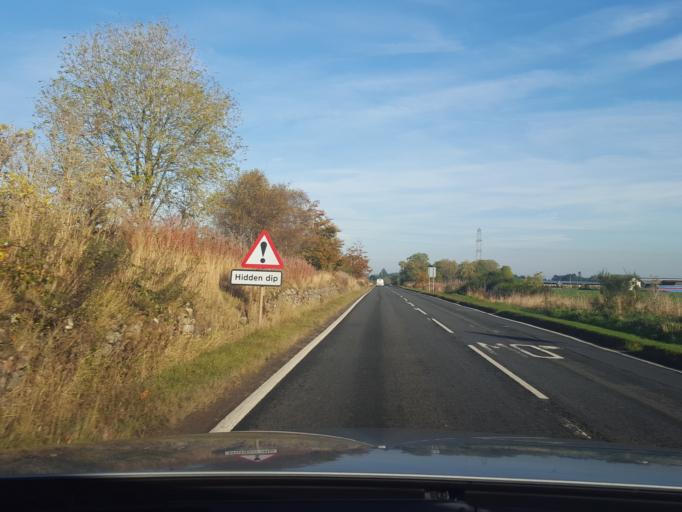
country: GB
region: Scotland
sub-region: Highland
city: Inverness
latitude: 57.4454
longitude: -4.2925
